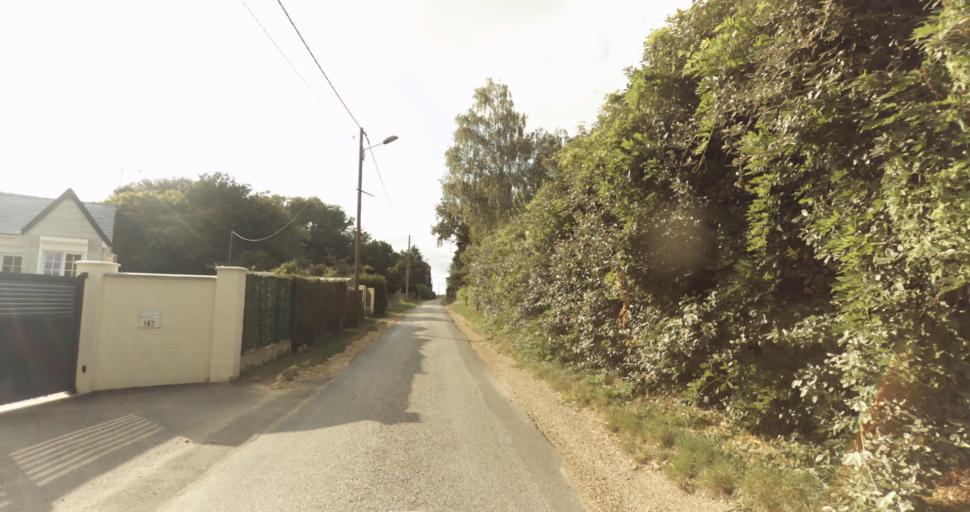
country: FR
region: Haute-Normandie
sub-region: Departement de l'Eure
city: La Couture-Boussey
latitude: 48.8922
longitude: 1.3759
